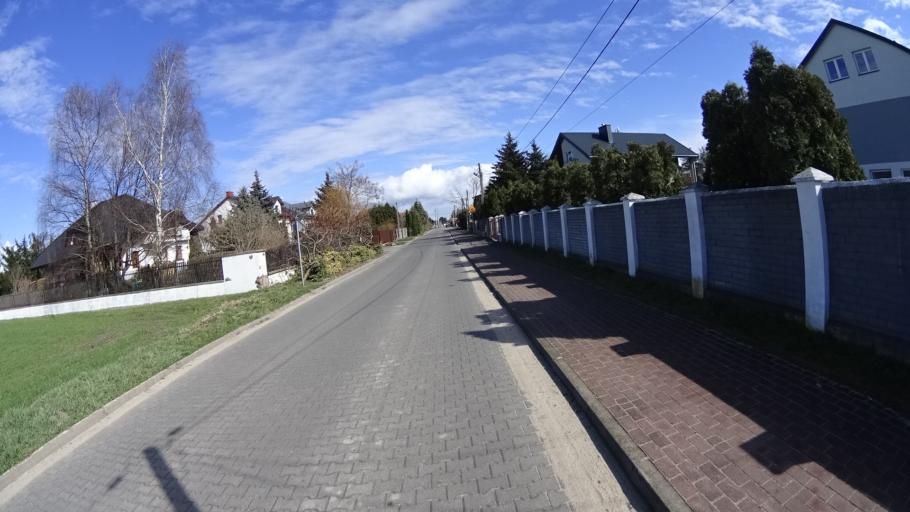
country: PL
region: Masovian Voivodeship
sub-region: Powiat warszawski zachodni
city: Jozefow
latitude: 52.2039
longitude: 20.7002
